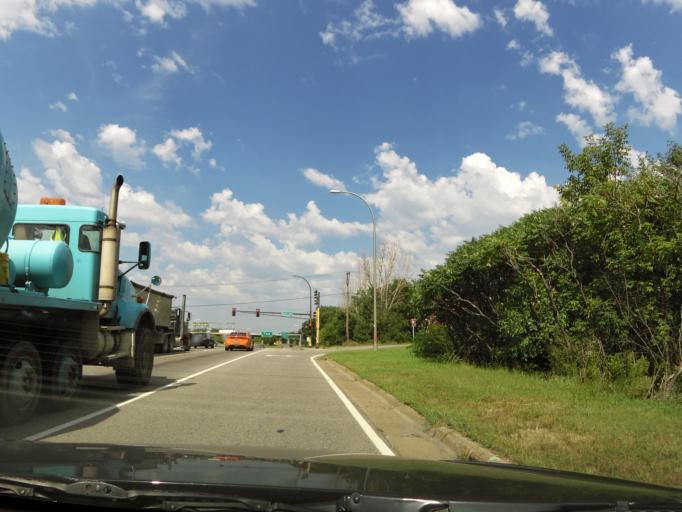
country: US
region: Minnesota
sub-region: Ramsey County
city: Maplewood
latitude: 44.9482
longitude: -93.0405
